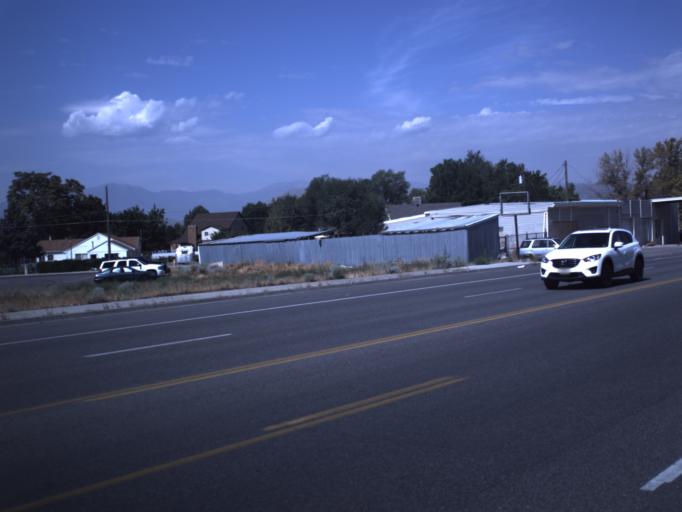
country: US
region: Utah
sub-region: Utah County
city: Lehi
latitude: 40.4028
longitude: -111.8558
